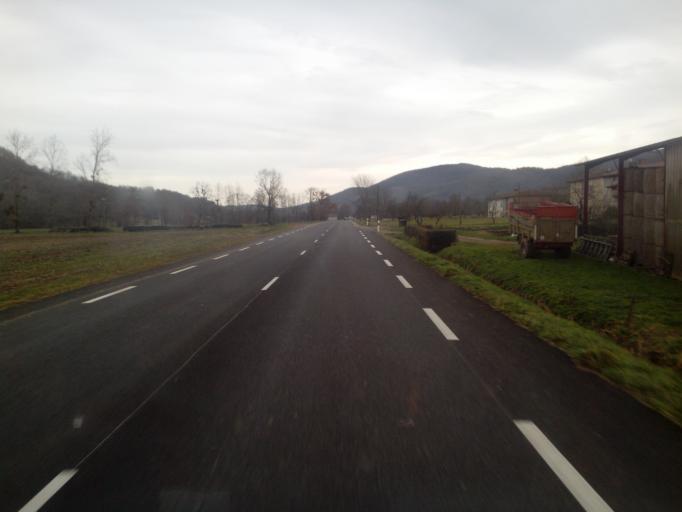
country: FR
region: Midi-Pyrenees
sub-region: Departement de l'Ariege
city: Foix
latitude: 43.0103
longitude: 1.4499
